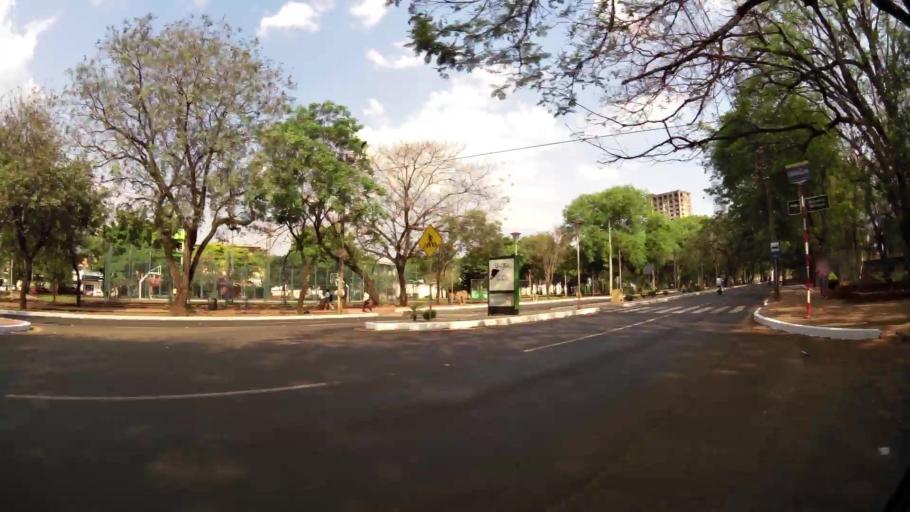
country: PY
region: Alto Parana
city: Presidente Franco
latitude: -25.5231
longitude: -54.6121
